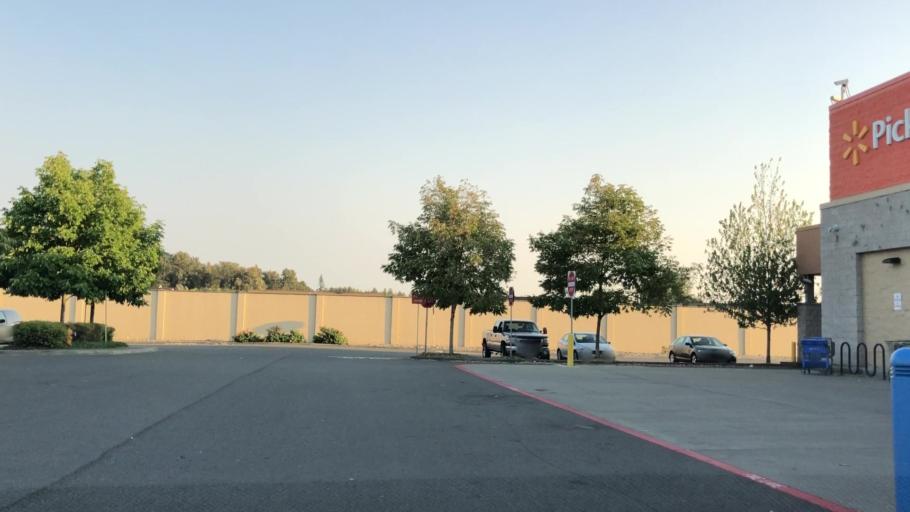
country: US
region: Washington
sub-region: Snohomish County
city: Smokey Point
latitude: 48.1500
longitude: -122.1746
